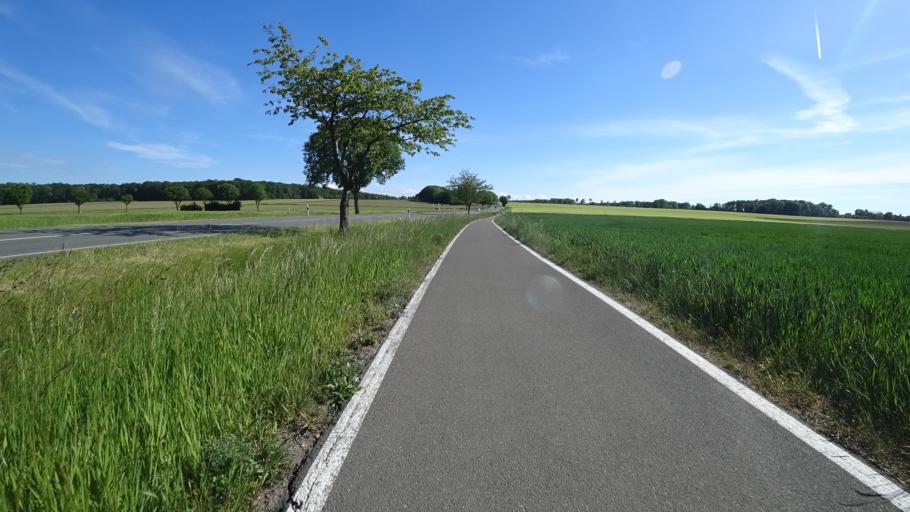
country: DE
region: North Rhine-Westphalia
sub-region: Regierungsbezirk Munster
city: Wadersloh
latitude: 51.7897
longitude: 8.2171
